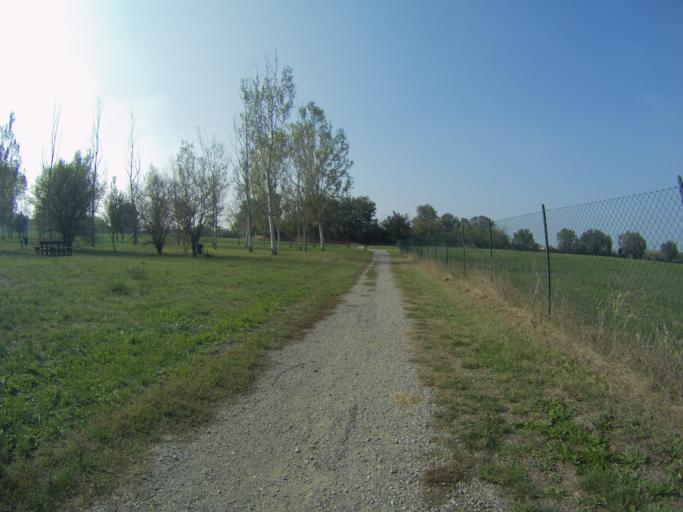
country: IT
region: Emilia-Romagna
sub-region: Provincia di Reggio Emilia
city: Albinea
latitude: 44.6585
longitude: 10.6003
